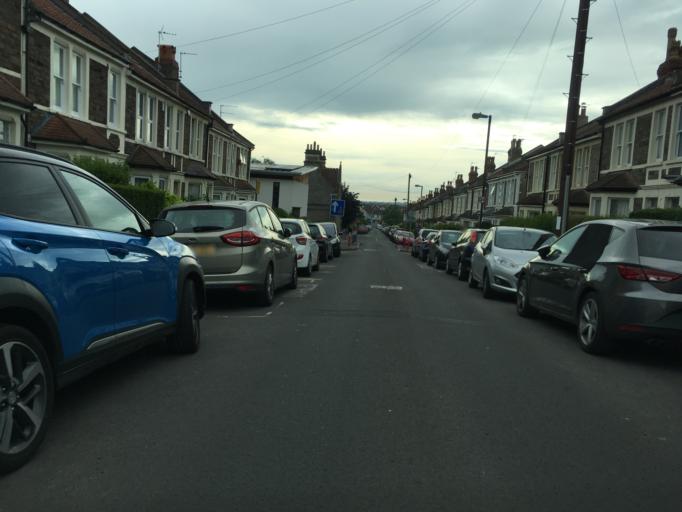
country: GB
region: England
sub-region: Bristol
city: Bristol
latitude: 51.4796
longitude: -2.5947
